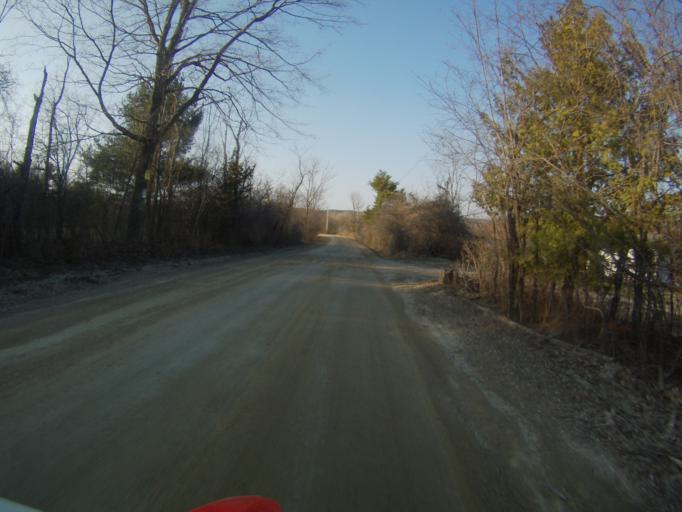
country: US
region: Vermont
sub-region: Addison County
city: Middlebury (village)
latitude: 44.0565
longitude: -73.1462
